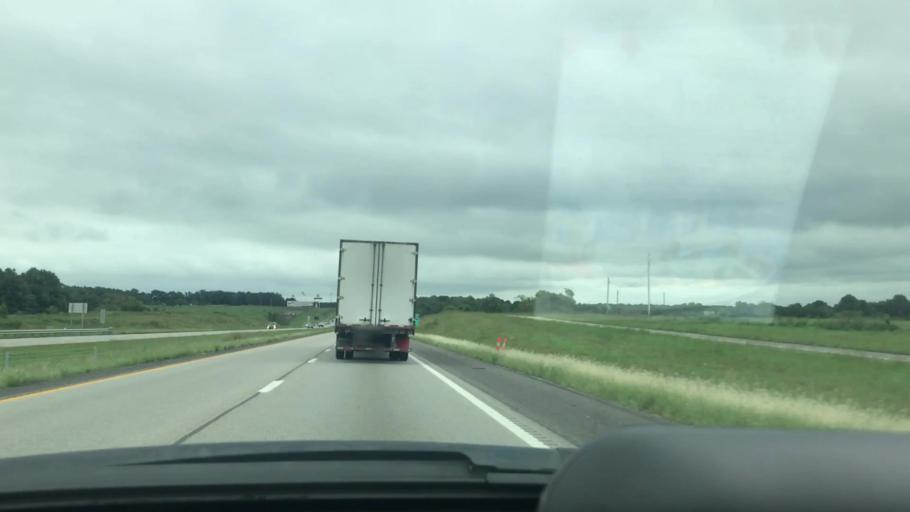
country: US
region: Missouri
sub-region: Christian County
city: Billings
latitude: 37.1859
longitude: -93.5847
